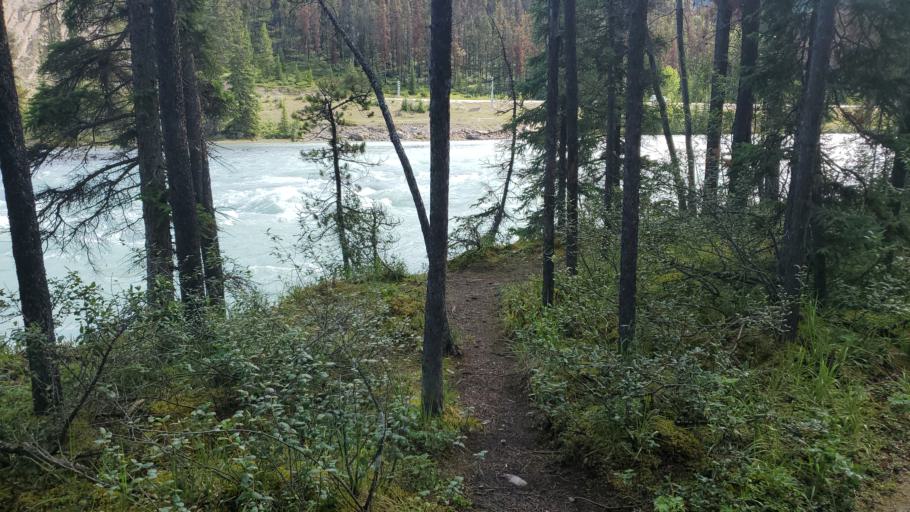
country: CA
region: Alberta
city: Jasper Park Lodge
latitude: 52.6637
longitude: -117.8818
